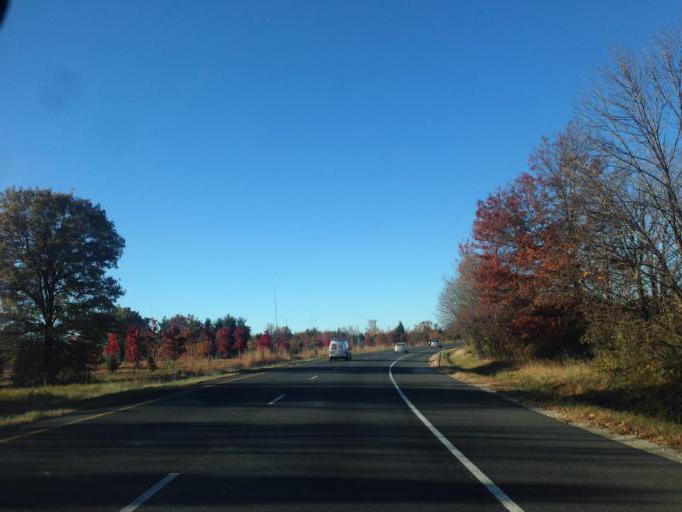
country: US
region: Maryland
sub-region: Baltimore County
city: Woodlawn
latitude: 39.3087
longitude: -76.7457
